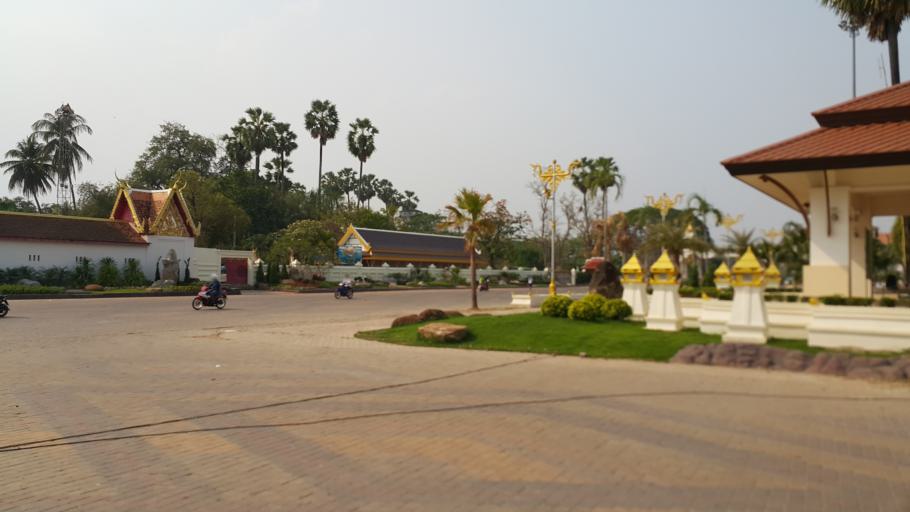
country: TH
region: Nakhon Phanom
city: That Phanom
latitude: 16.9426
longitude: 104.7251
